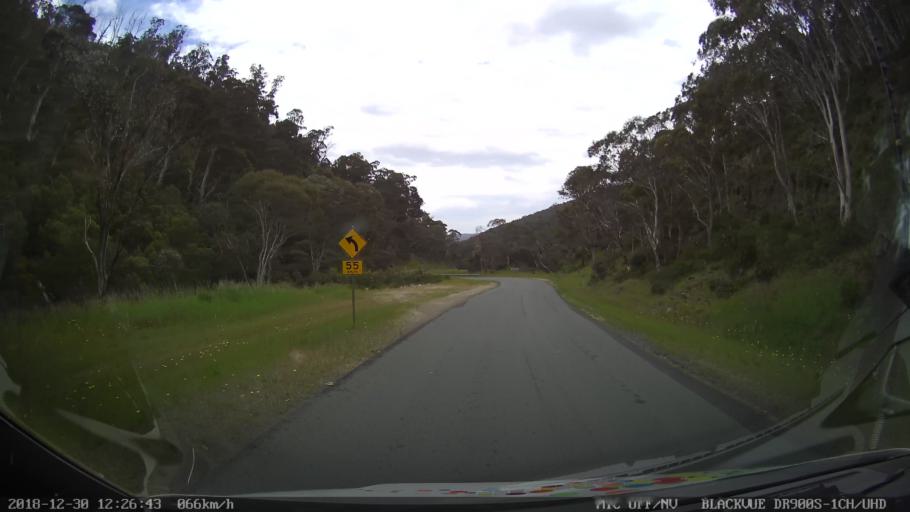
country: AU
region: New South Wales
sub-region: Snowy River
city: Jindabyne
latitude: -36.3363
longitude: 148.4895
